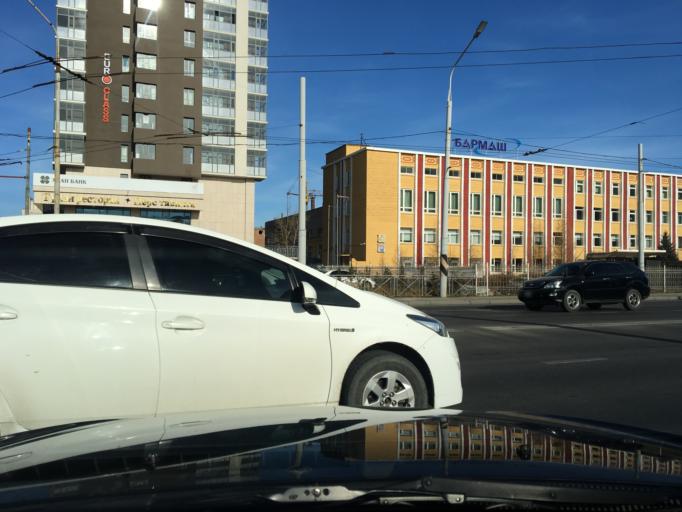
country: MN
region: Ulaanbaatar
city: Ulaanbaatar
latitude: 47.8962
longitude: 106.8851
